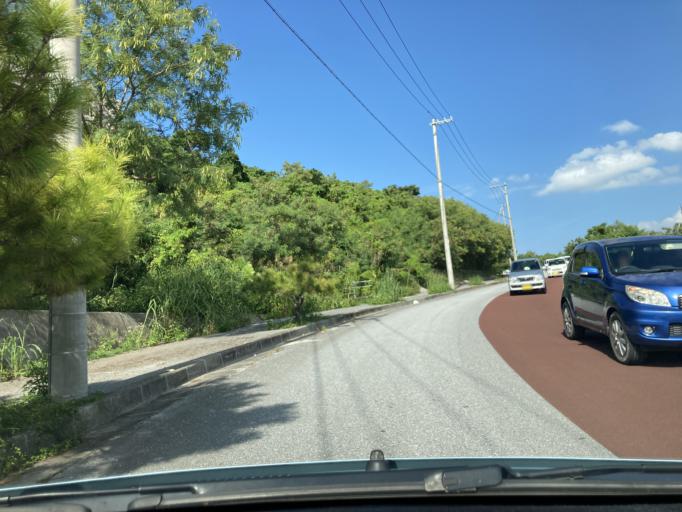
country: JP
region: Okinawa
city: Ginowan
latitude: 26.2780
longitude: 127.7975
